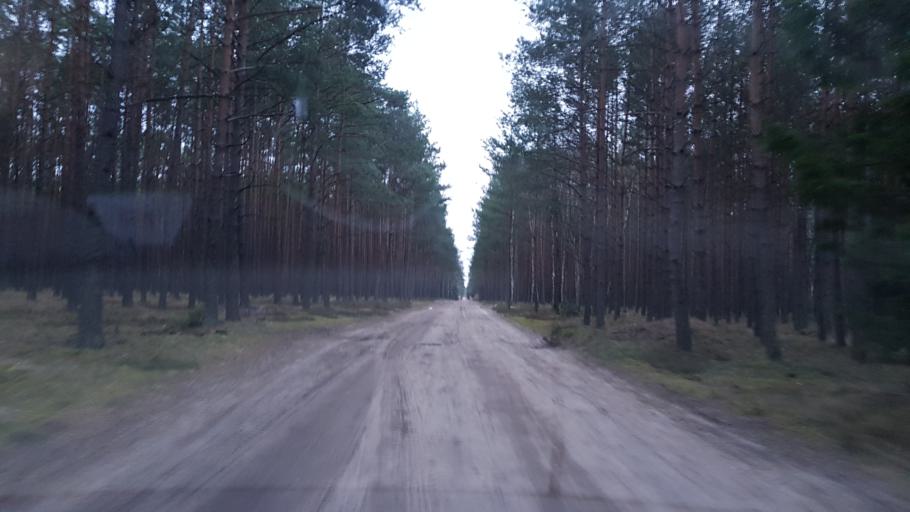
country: PL
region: Greater Poland Voivodeship
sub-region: Powiat zlotowski
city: Sypniewo
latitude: 53.5019
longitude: 16.6754
